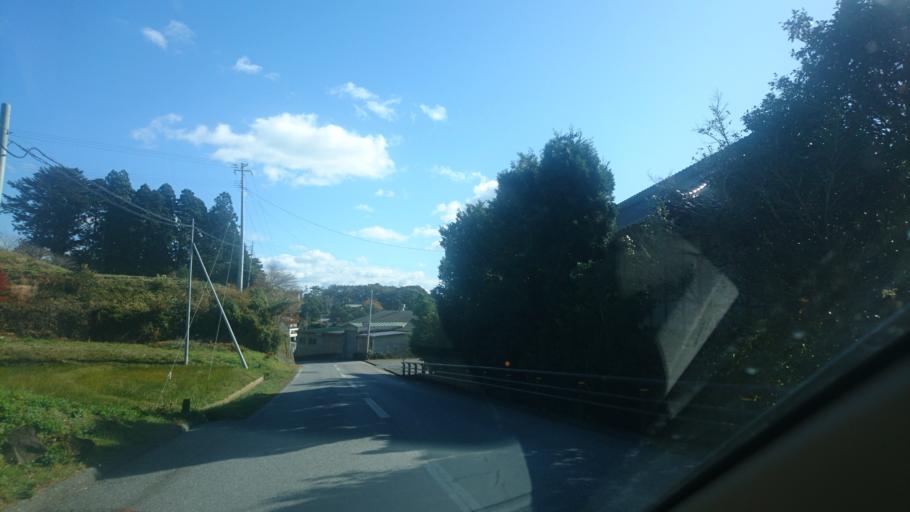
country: JP
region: Iwate
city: Ofunato
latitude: 38.9896
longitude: 141.7352
